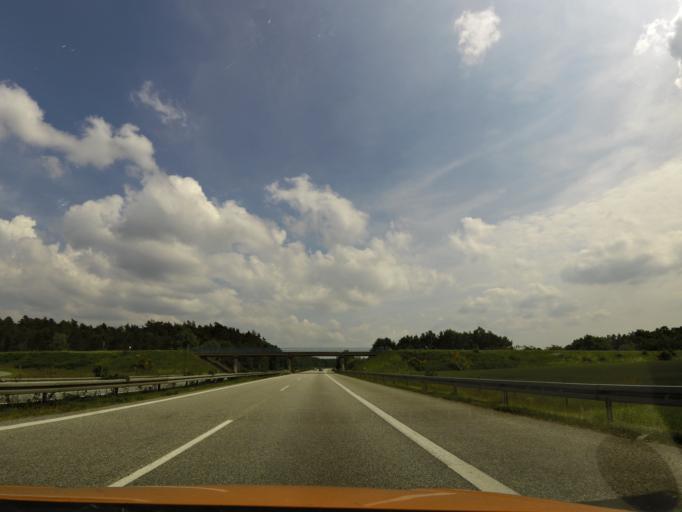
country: DE
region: Mecklenburg-Vorpommern
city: Spornitz
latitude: 53.3637
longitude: 11.7471
